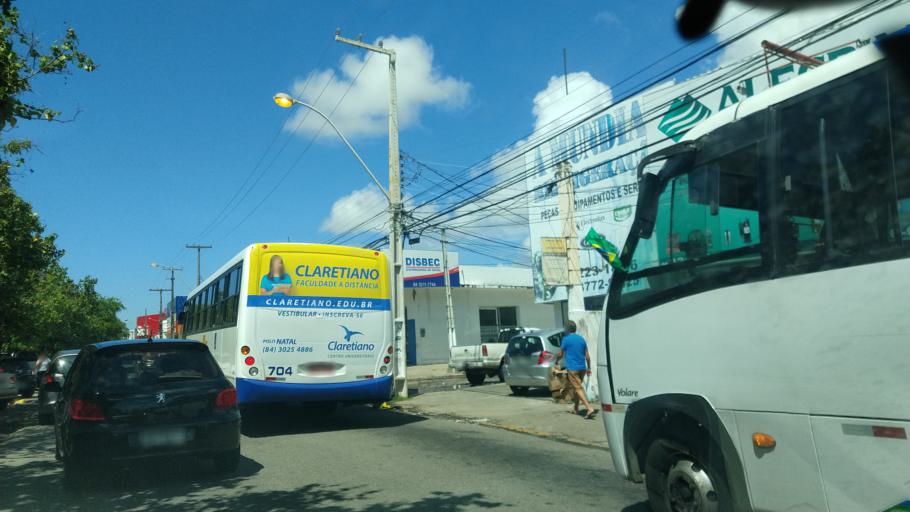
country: BR
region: Rio Grande do Norte
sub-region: Natal
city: Natal
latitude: -5.8011
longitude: -35.2157
